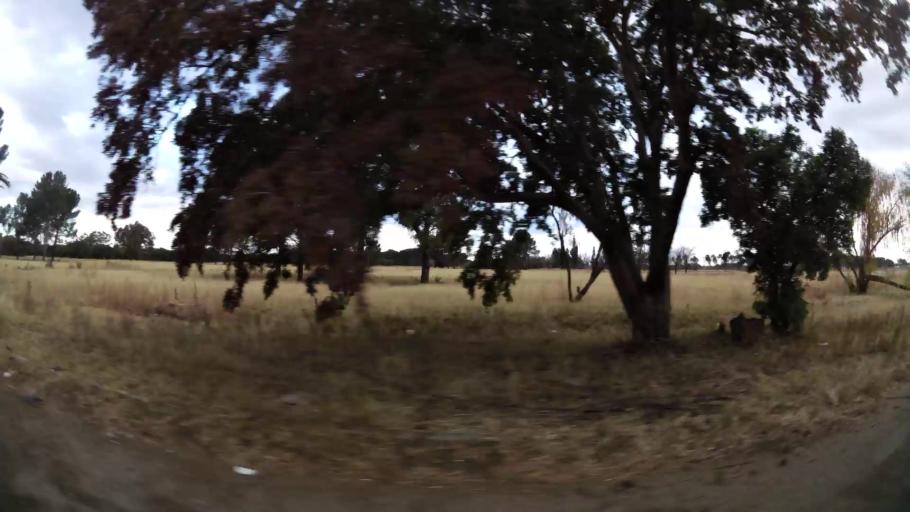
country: ZA
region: Orange Free State
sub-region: Lejweleputswa District Municipality
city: Welkom
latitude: -27.9633
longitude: 26.7161
